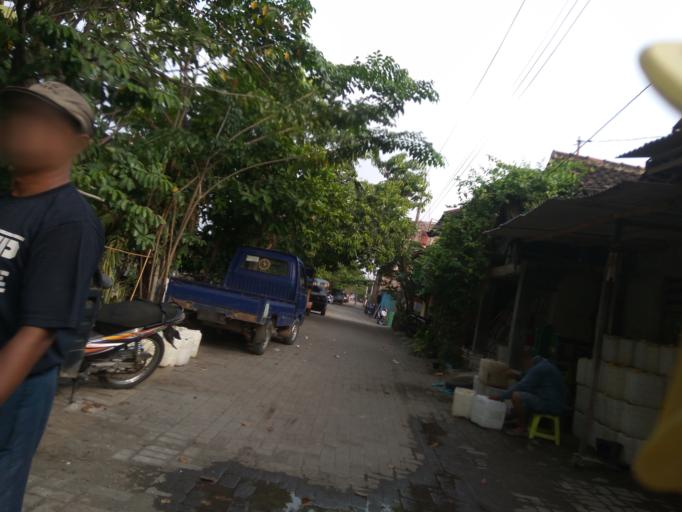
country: ID
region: Central Java
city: Semarang
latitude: -6.9705
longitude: 110.3928
